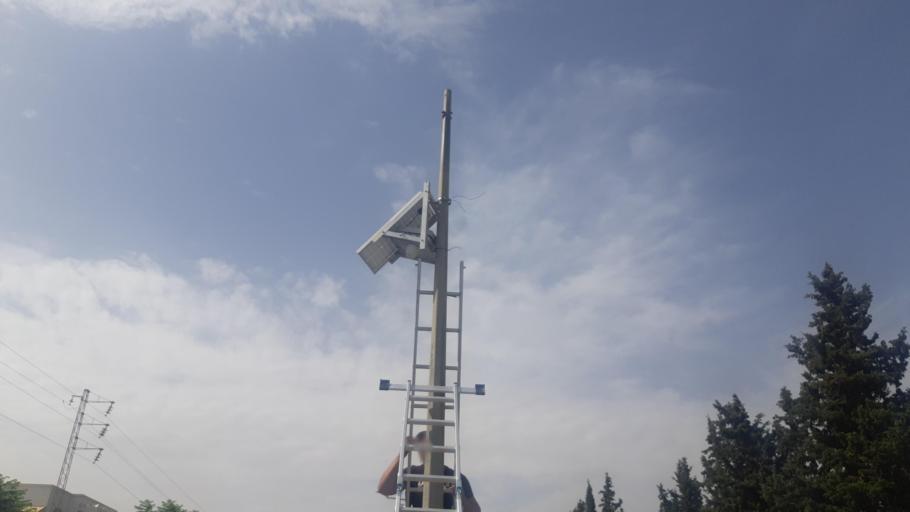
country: TN
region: Al Mahdiyah
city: Zouila
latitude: 35.5082
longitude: 11.0248
